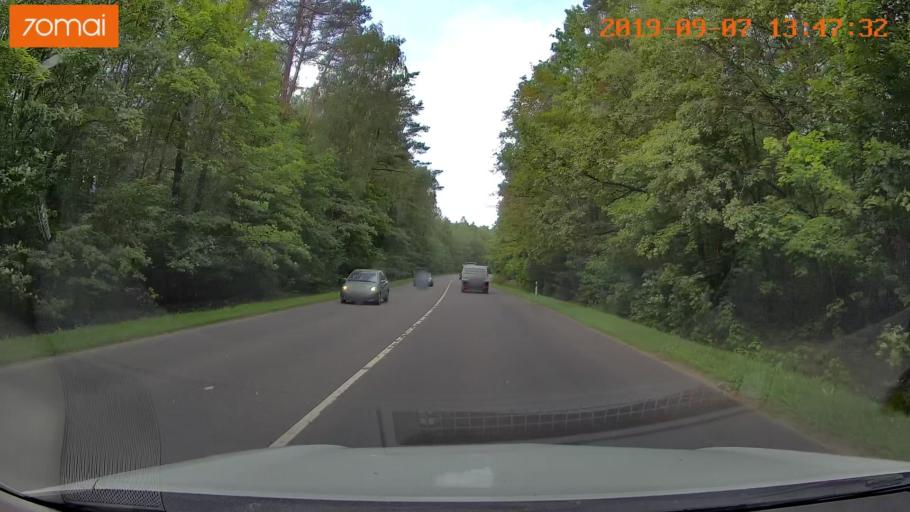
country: LT
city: Baltoji Voke
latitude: 54.5978
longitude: 25.2135
